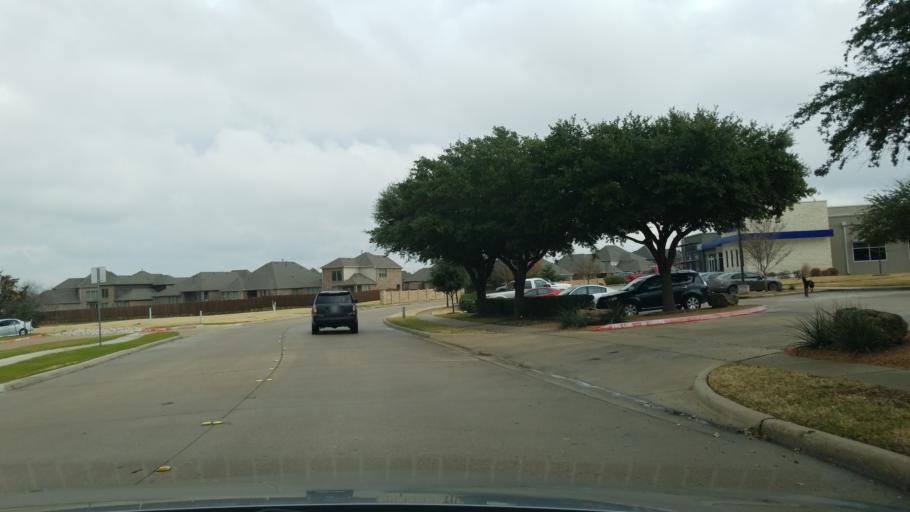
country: US
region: Texas
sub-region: Denton County
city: Lewisville
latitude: 33.0453
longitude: -97.0194
